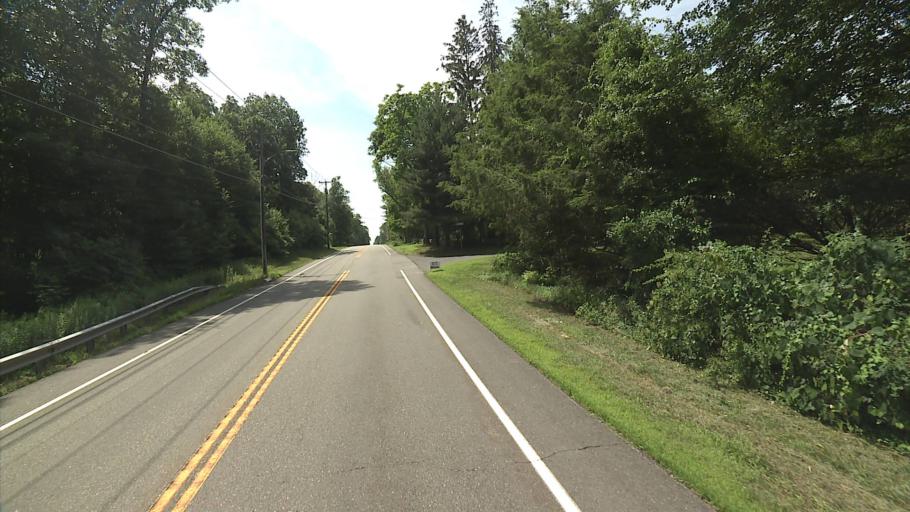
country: US
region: Connecticut
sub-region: Tolland County
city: Tolland
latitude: 41.8239
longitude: -72.3982
